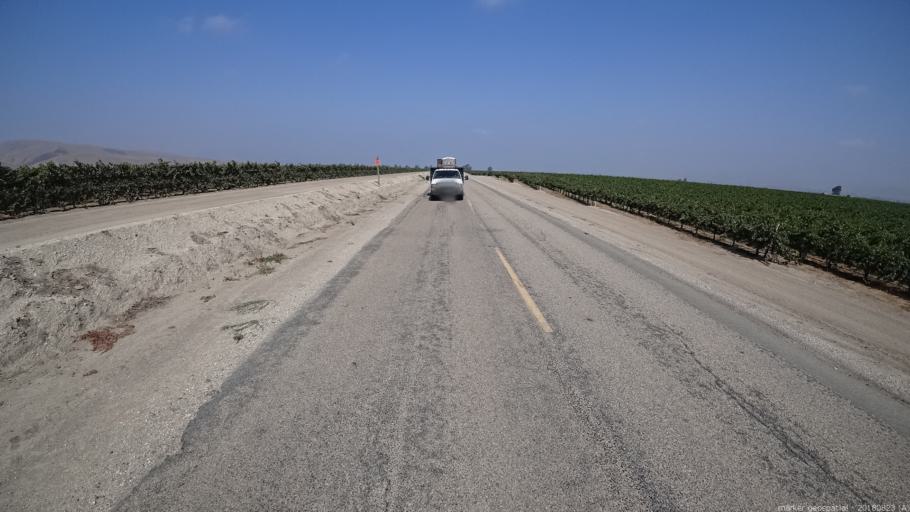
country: US
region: California
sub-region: Monterey County
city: Greenfield
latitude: 36.2680
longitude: -121.2165
